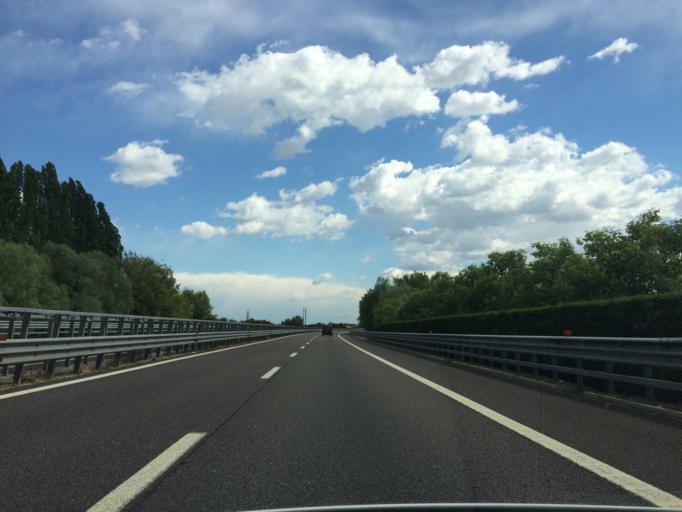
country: IT
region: Veneto
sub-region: Provincia di Vicenza
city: Villaggio Montegrappa
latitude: 45.5490
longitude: 11.6192
